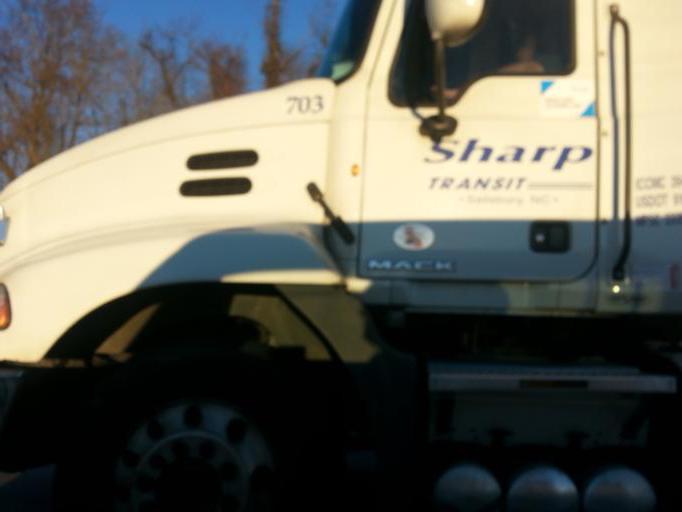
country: US
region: North Carolina
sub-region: Buncombe County
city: Avery Creek
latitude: 35.4675
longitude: -82.5495
